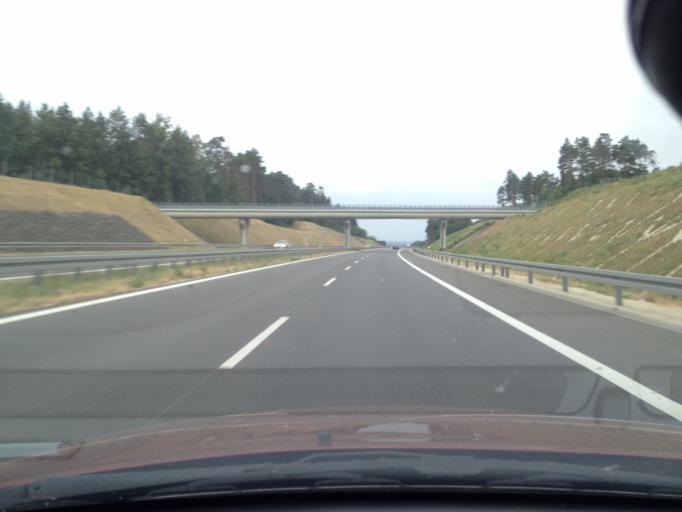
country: PL
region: Lubusz
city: Gorzow Wielkopolski
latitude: 52.7309
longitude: 15.1643
